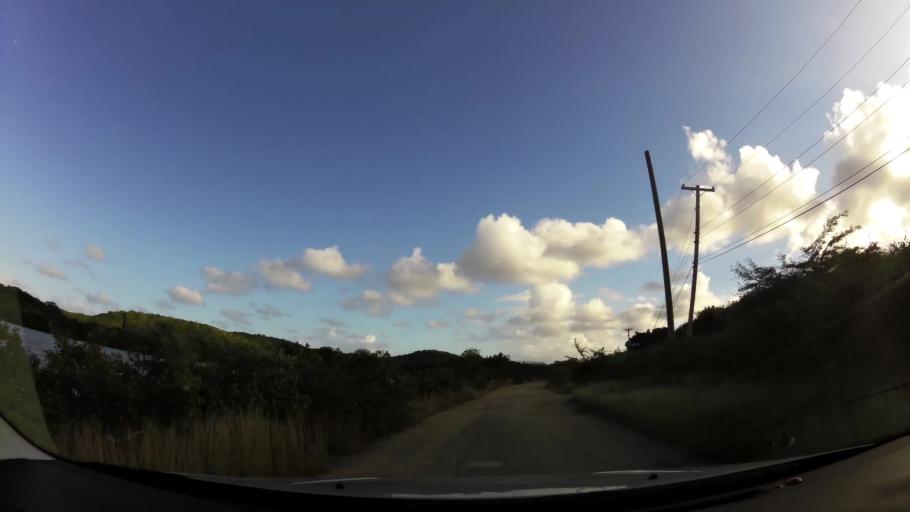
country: AG
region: Saint George
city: Piggotts
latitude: 17.1233
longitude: -61.7878
